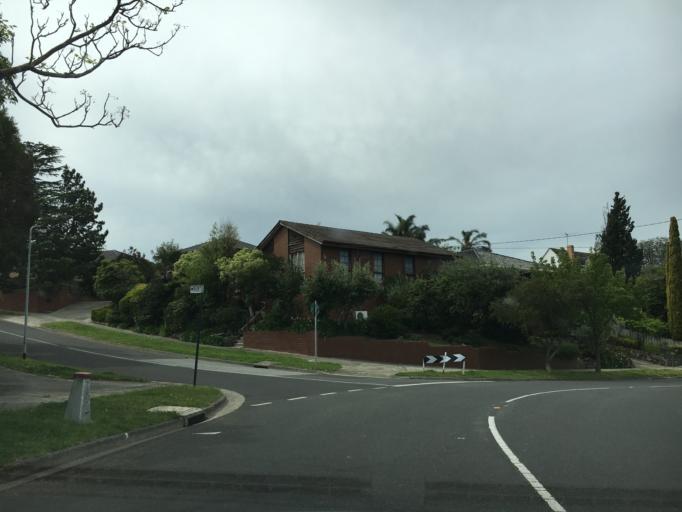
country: AU
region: Victoria
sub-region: Monash
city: Chadstone
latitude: -37.8895
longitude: 145.1023
